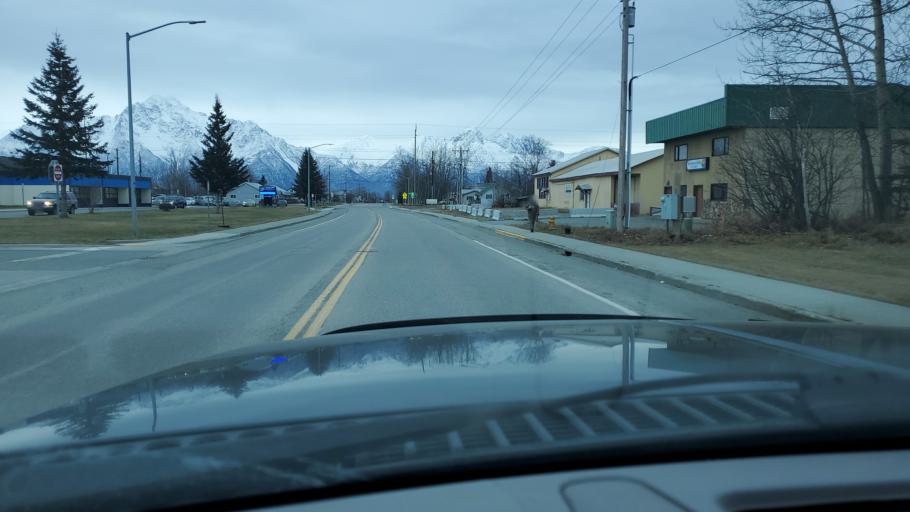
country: US
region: Alaska
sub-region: Matanuska-Susitna Borough
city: Palmer
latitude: 61.5938
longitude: -149.1108
